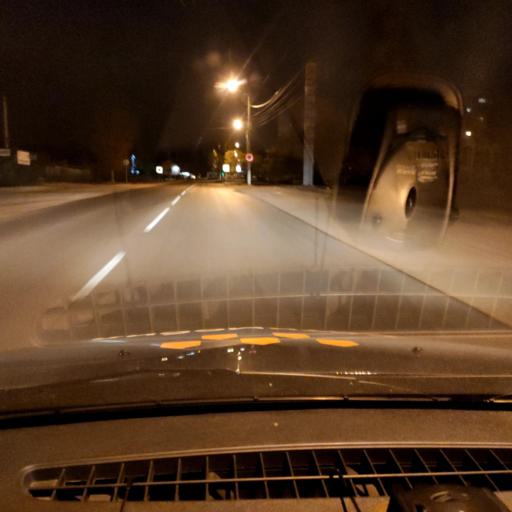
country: RU
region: Voronezj
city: Shilovo
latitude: 51.5497
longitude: 39.0874
